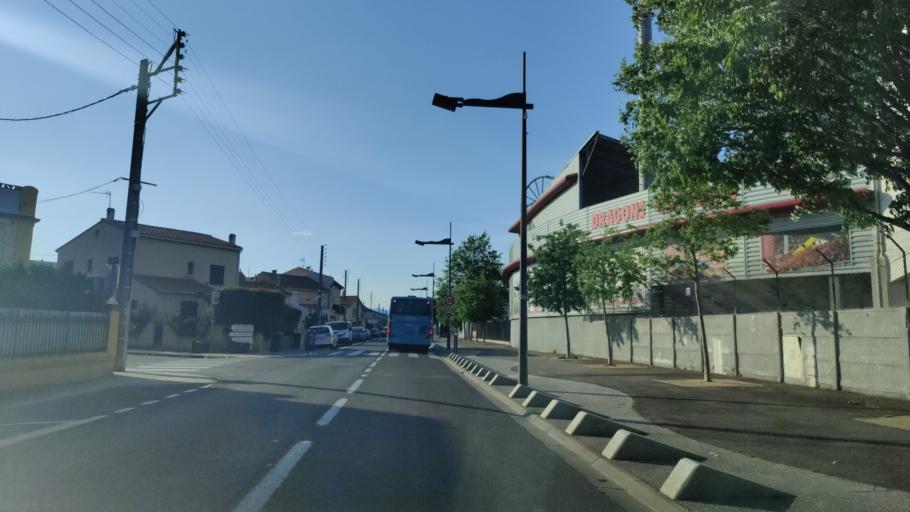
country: FR
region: Languedoc-Roussillon
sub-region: Departement des Pyrenees-Orientales
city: Perpignan
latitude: 42.7224
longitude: 2.8846
